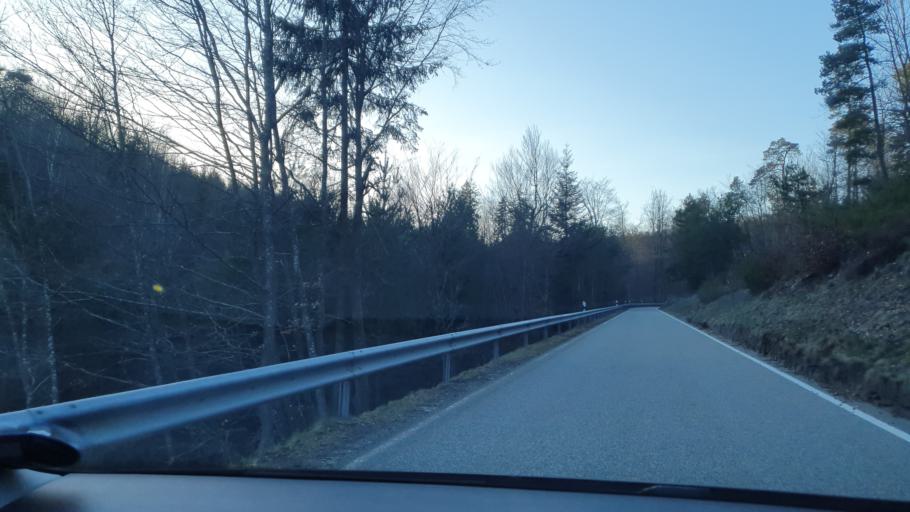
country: DE
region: Rheinland-Pfalz
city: Waldleiningen
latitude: 49.3985
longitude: 7.8537
